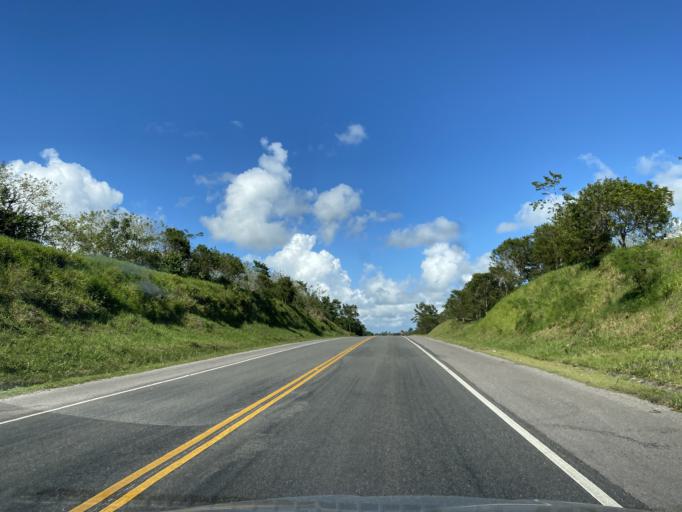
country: DO
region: Monte Plata
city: Majagual
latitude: 19.0170
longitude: -69.8228
